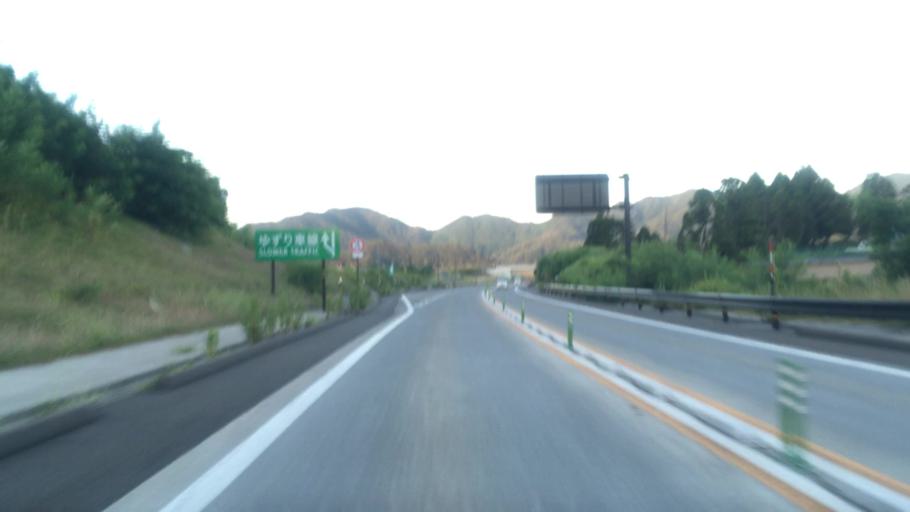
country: JP
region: Tottori
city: Tottori
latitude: 35.5492
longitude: 134.2672
